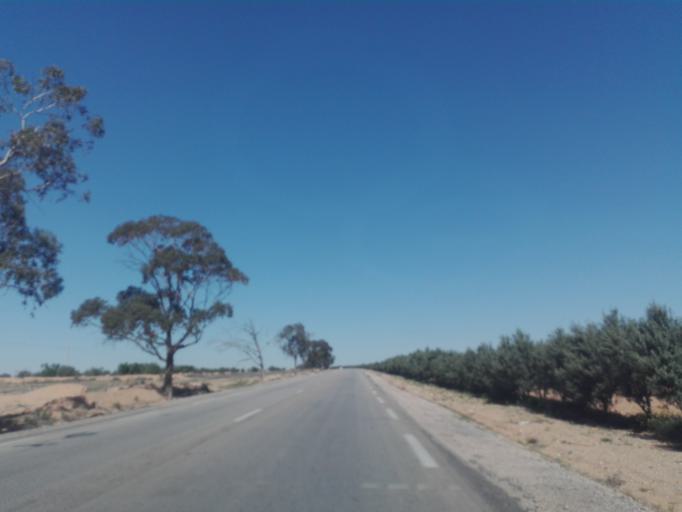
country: TN
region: Safaqis
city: Bi'r `Ali Bin Khalifah
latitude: 34.7492
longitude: 10.3504
